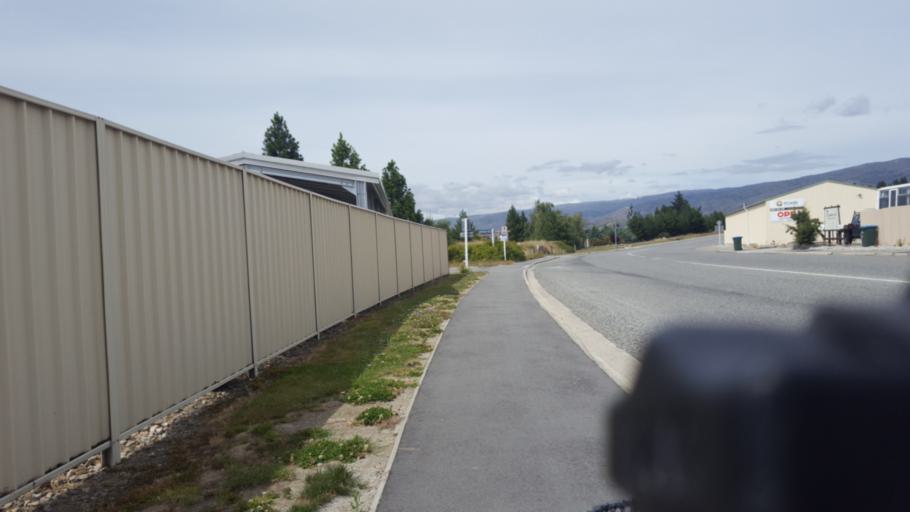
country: NZ
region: Otago
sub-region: Queenstown-Lakes District
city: Wanaka
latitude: -45.0522
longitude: 169.1958
